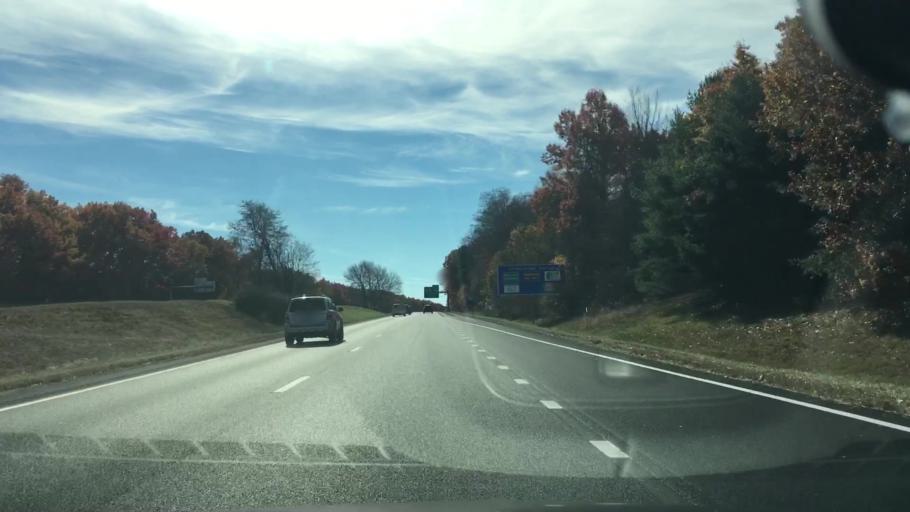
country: US
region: Massachusetts
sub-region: Hampshire County
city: Northampton
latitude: 42.3590
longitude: -72.6376
